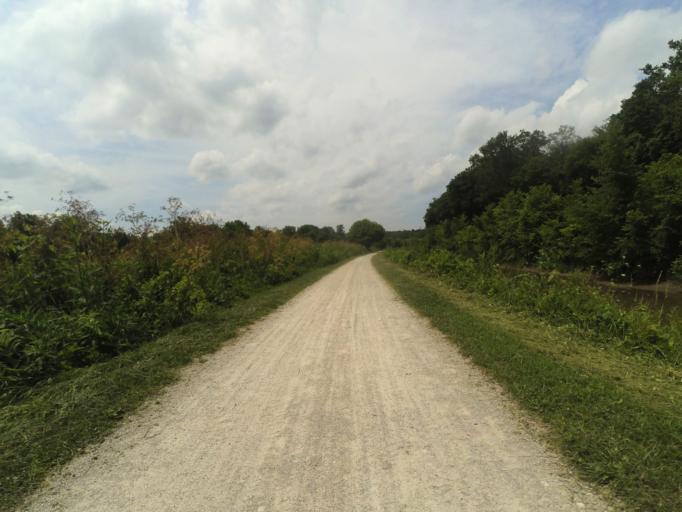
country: US
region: Ohio
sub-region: Cuyahoga County
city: Valley View
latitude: 41.3625
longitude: -81.6037
